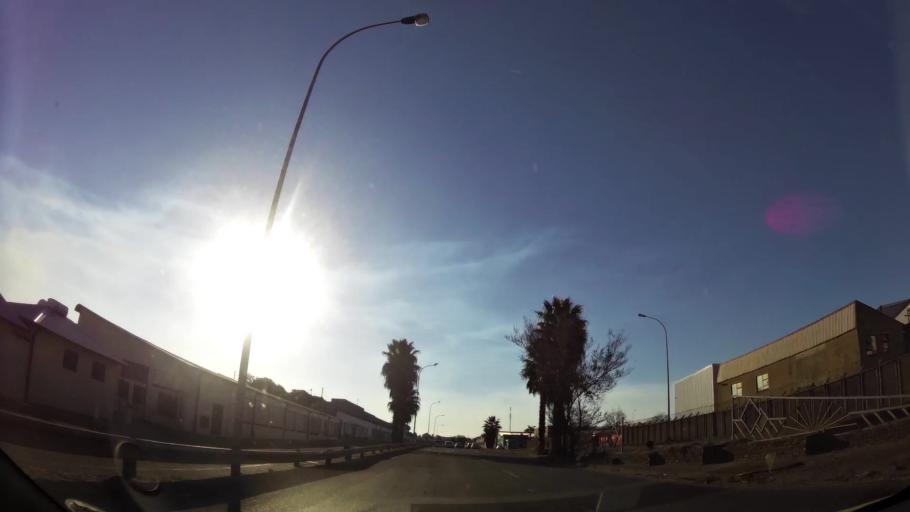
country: ZA
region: Gauteng
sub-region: City of Johannesburg Metropolitan Municipality
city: Roodepoort
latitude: -26.1541
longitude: 27.8661
